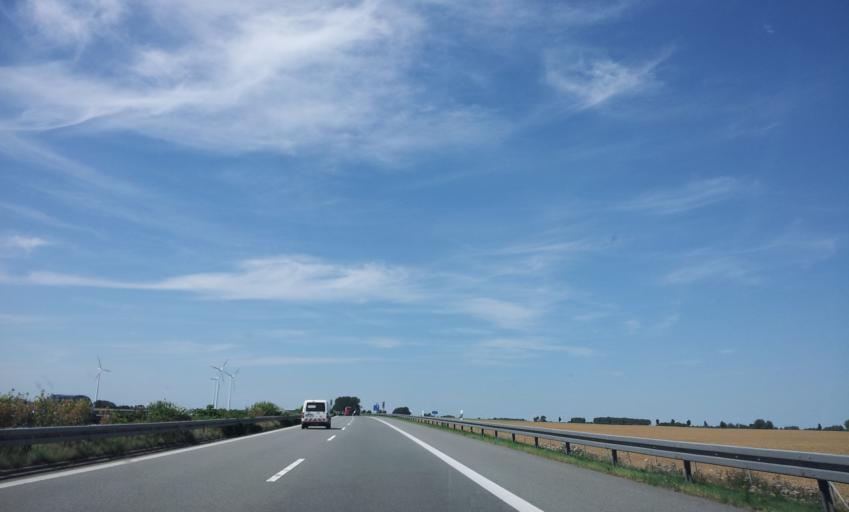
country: DE
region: Mecklenburg-Vorpommern
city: Jarmen
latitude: 53.9893
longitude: 13.3393
